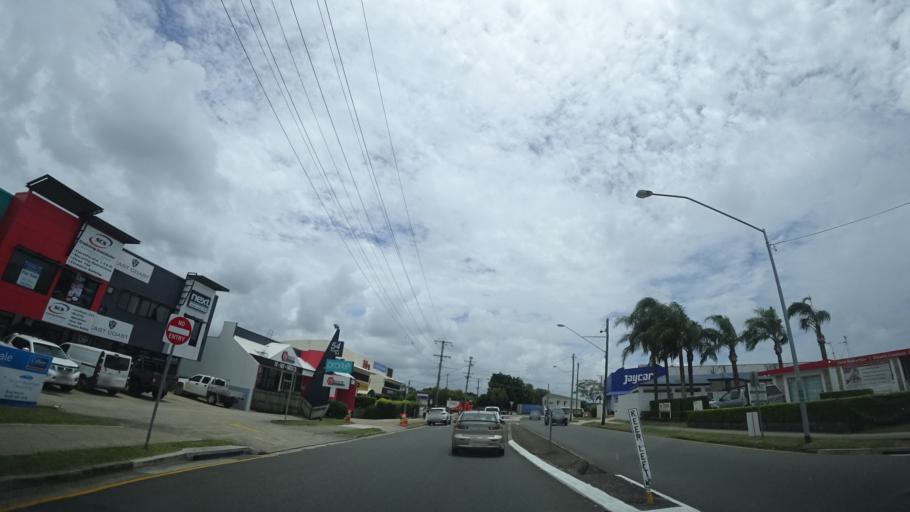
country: AU
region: Queensland
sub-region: Sunshine Coast
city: Mooloolaba
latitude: -26.6669
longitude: 153.0928
